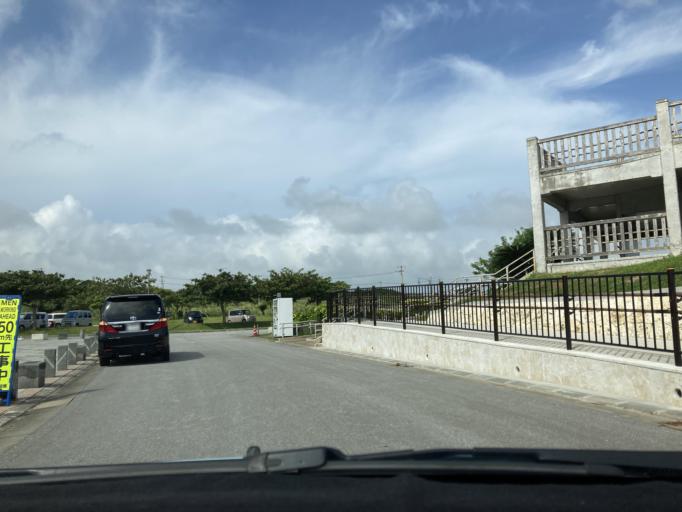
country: JP
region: Okinawa
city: Itoman
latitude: 26.0981
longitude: 127.7267
